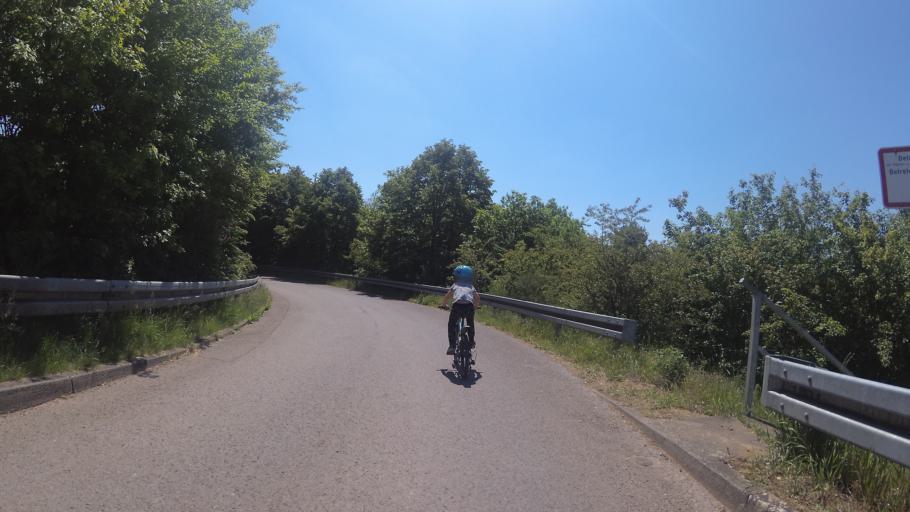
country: DE
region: Saarland
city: Mettlach
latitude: 49.4678
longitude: 6.6059
